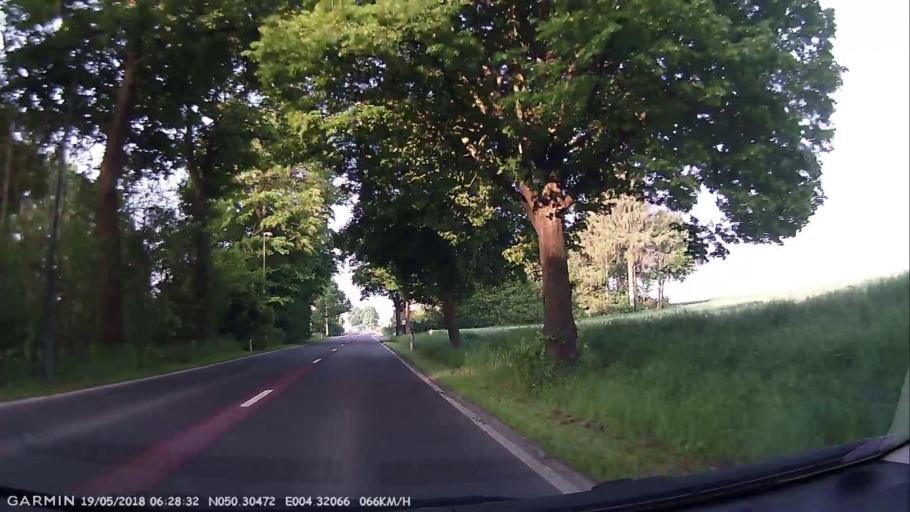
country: BE
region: Wallonia
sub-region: Province du Hainaut
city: Thuin
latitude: 50.3047
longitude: 4.3206
